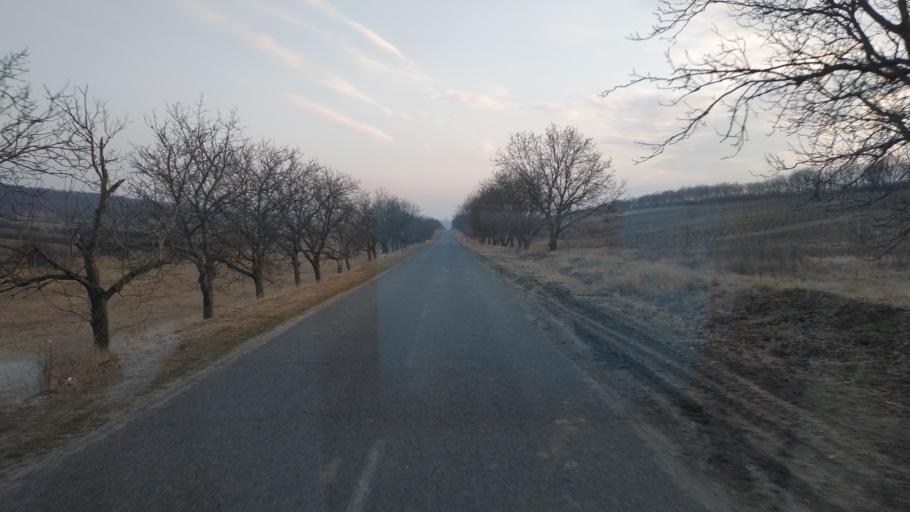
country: MD
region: Hincesti
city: Dancu
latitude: 46.6896
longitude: 28.3359
